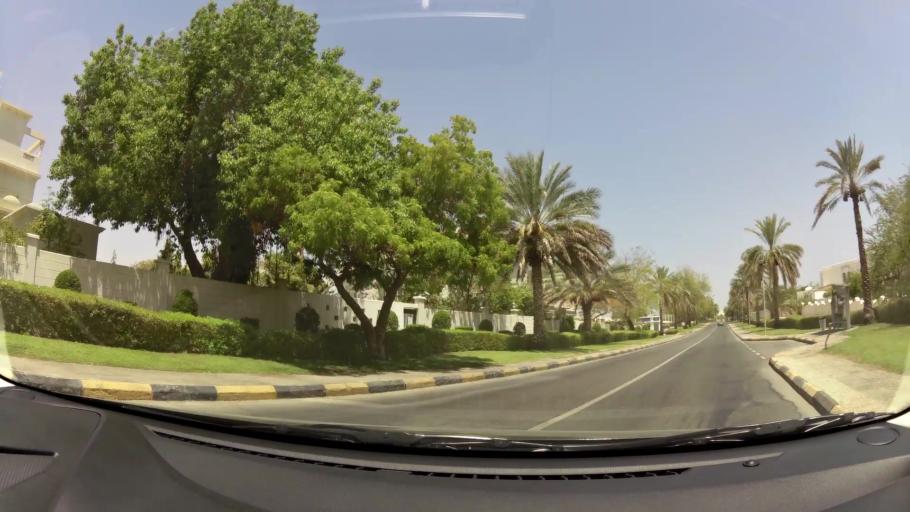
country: OM
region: Muhafazat Masqat
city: Bawshar
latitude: 23.5995
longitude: 58.4715
